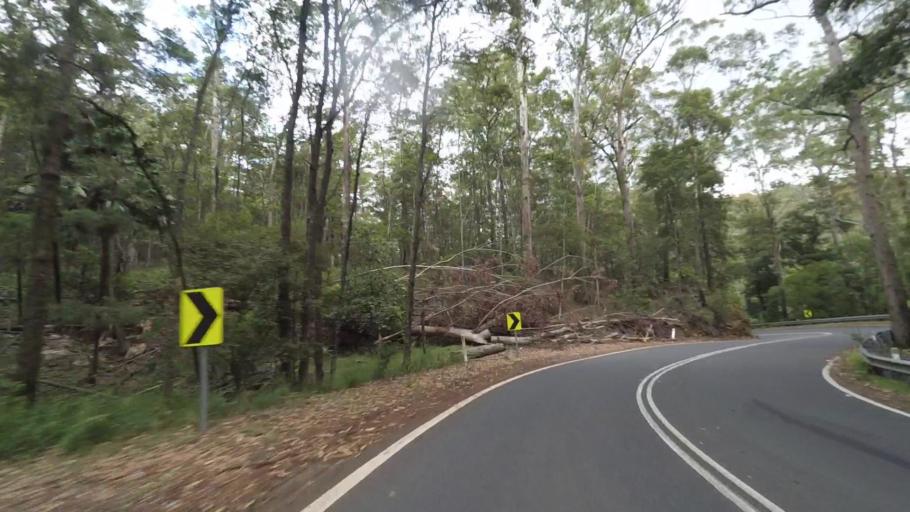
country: AU
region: New South Wales
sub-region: Wollongong
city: Helensburgh
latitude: -34.1497
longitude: 151.0292
